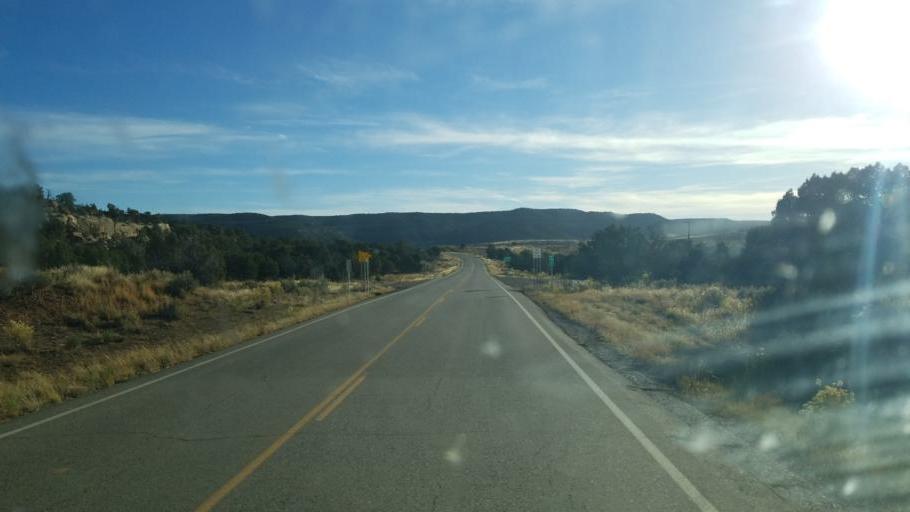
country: US
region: New Mexico
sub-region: San Juan County
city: Bloomfield
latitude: 36.7487
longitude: -107.6173
